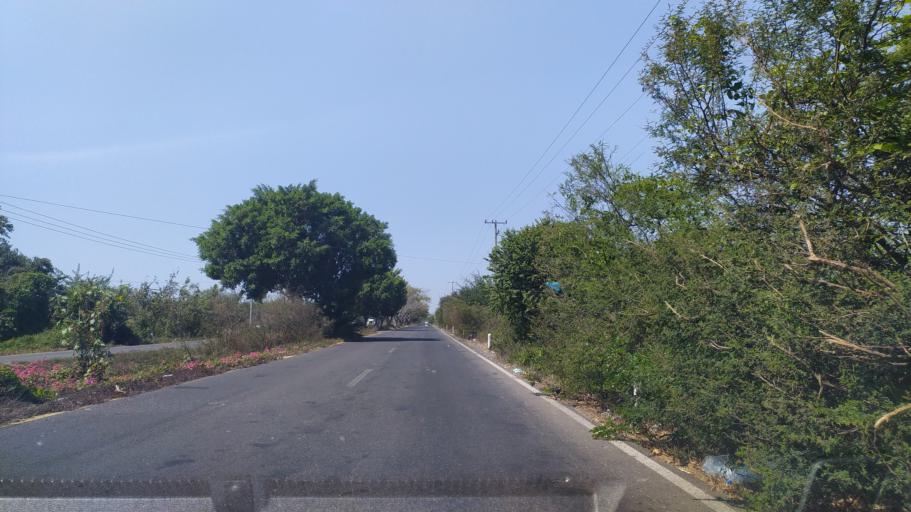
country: MX
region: Colima
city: Tecoman
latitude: 18.9369
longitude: -103.8719
